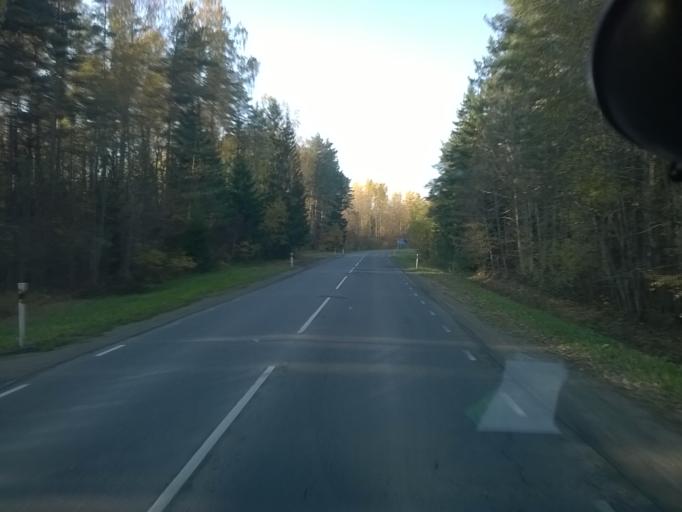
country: EE
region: Harju
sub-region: Saku vald
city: Saku
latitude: 59.3124
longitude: 24.6764
